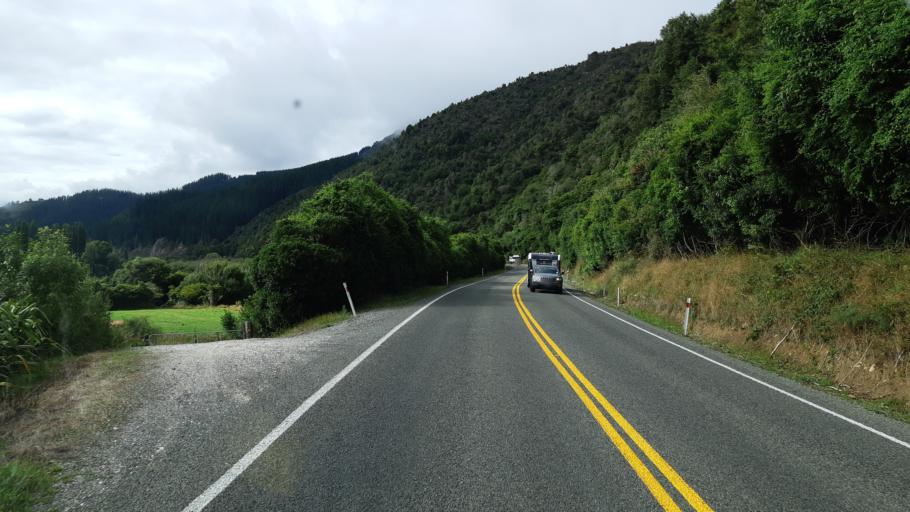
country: NZ
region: West Coast
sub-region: Buller District
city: Westport
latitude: -41.7720
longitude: 172.2378
